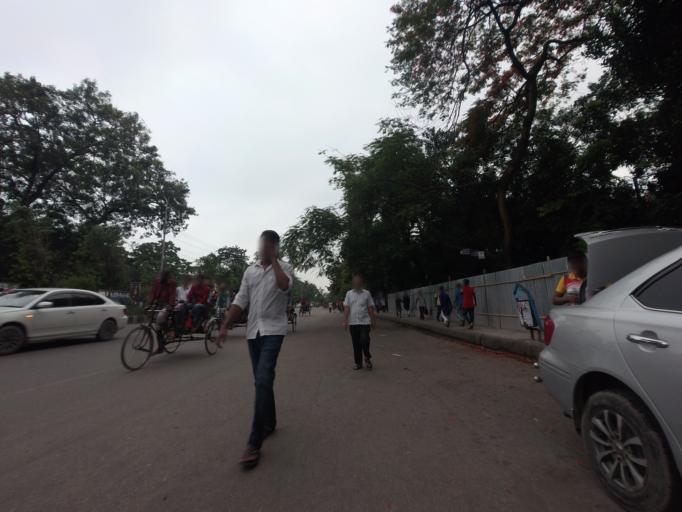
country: BD
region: Dhaka
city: Azimpur
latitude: 23.7366
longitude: 90.3954
